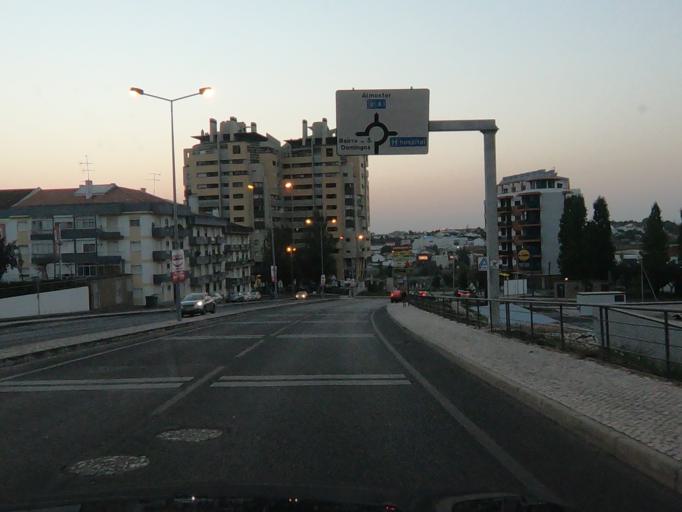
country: PT
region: Santarem
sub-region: Santarem
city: Santarem
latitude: 39.2379
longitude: -8.6967
